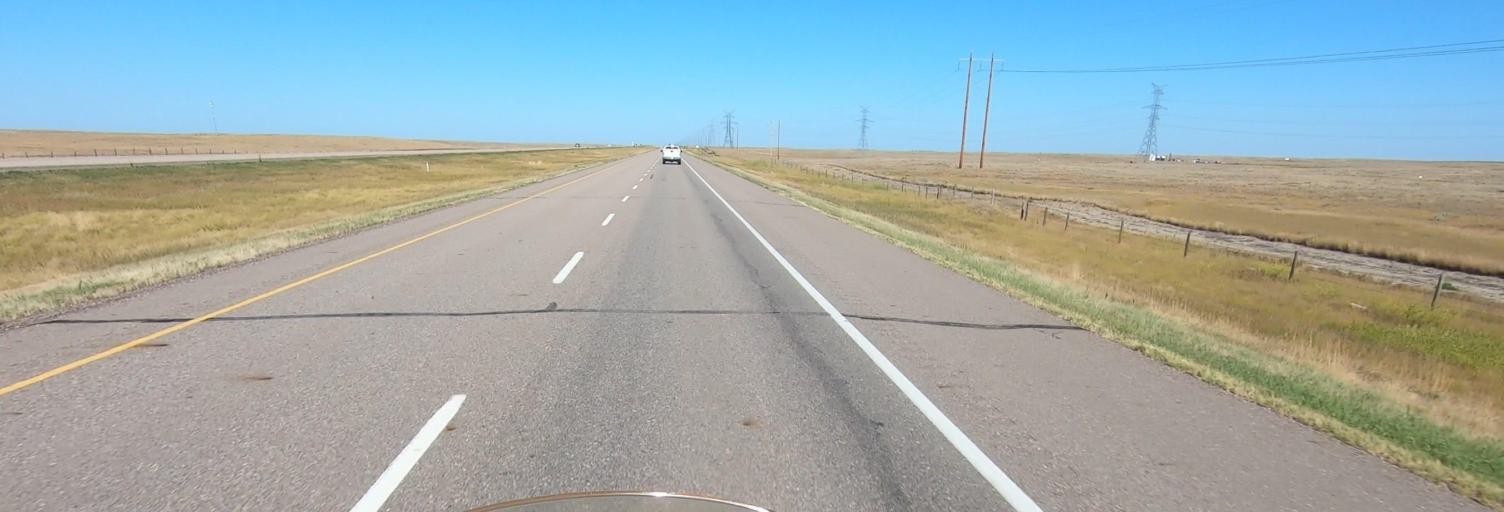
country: CA
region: Alberta
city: Bow Island
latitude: 50.3641
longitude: -111.4248
